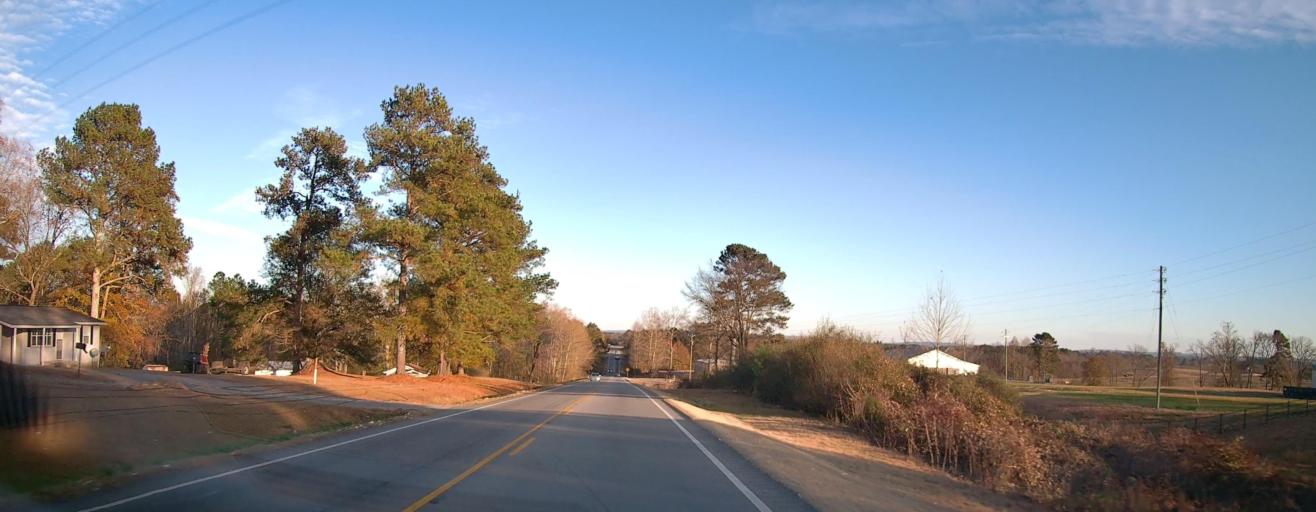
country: US
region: Alabama
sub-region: Blount County
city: Blountsville
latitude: 34.1372
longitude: -86.4327
